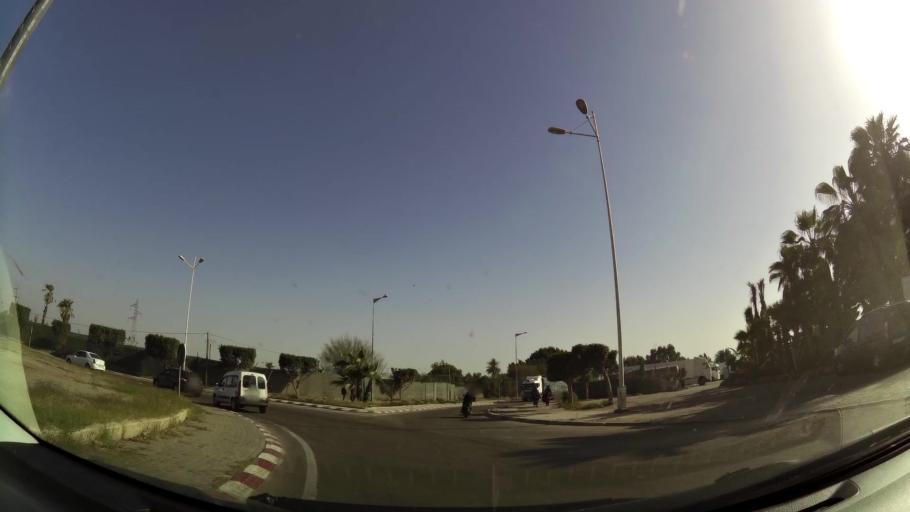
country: MA
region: Souss-Massa-Draa
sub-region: Inezgane-Ait Mellou
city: Inezgane
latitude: 30.3715
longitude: -9.5054
